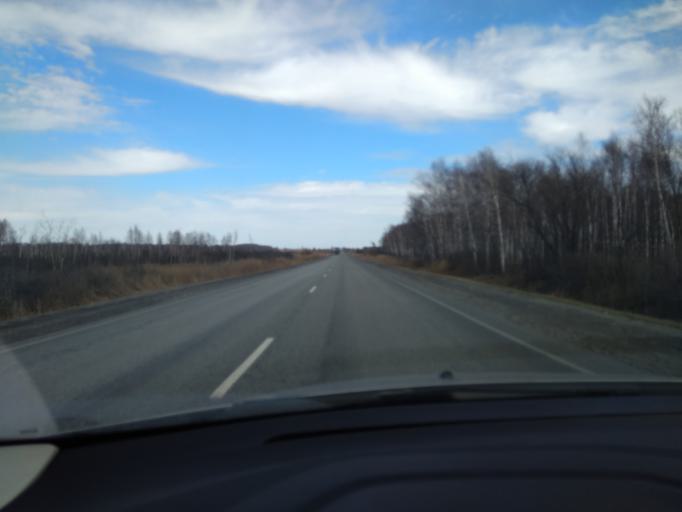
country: RU
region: Sverdlovsk
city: Pyshma
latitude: 56.9888
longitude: 63.2682
